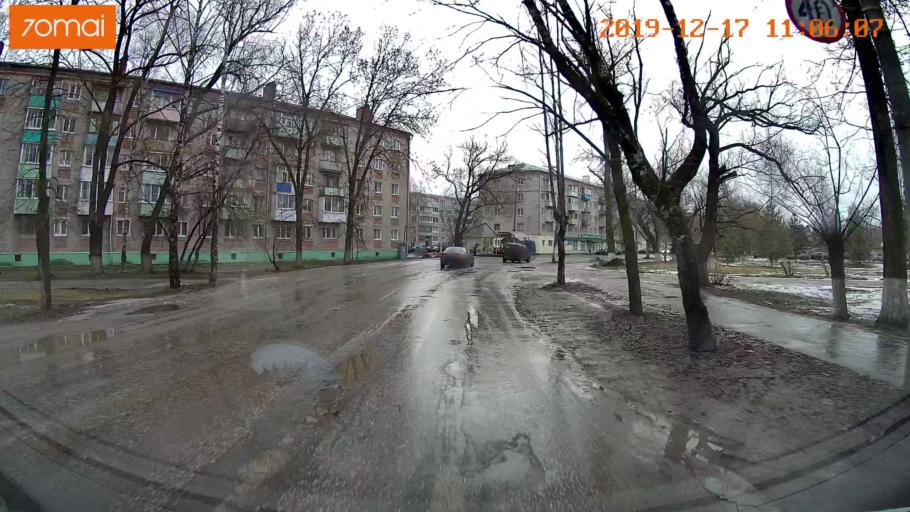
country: RU
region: Vladimir
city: Gus'-Khrustal'nyy
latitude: 55.6171
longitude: 40.6441
